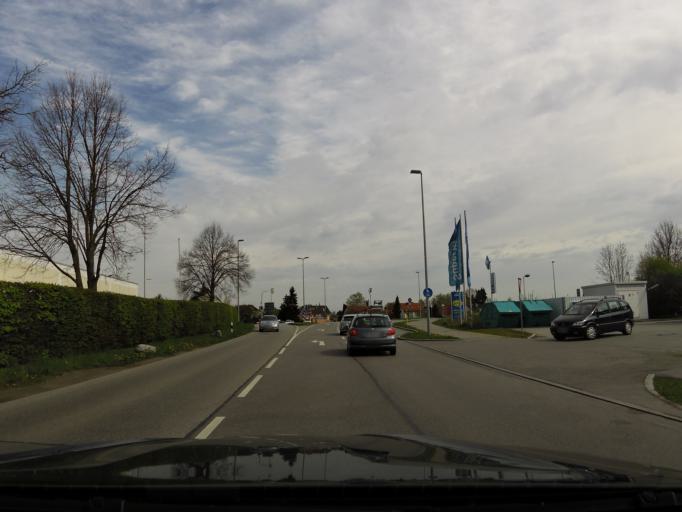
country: DE
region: Bavaria
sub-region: Upper Bavaria
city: Erding
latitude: 48.3148
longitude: 11.8926
